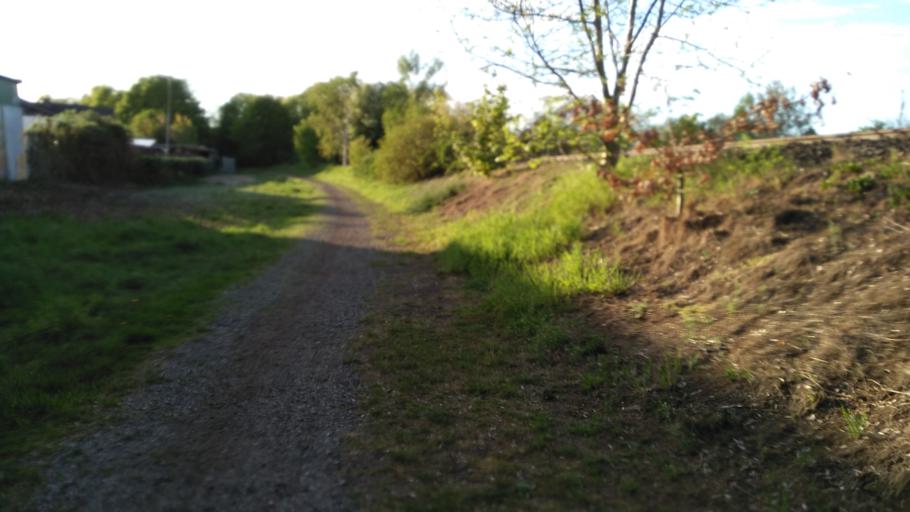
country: DE
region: Lower Saxony
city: Buxtehude
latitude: 53.4679
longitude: 9.7031
